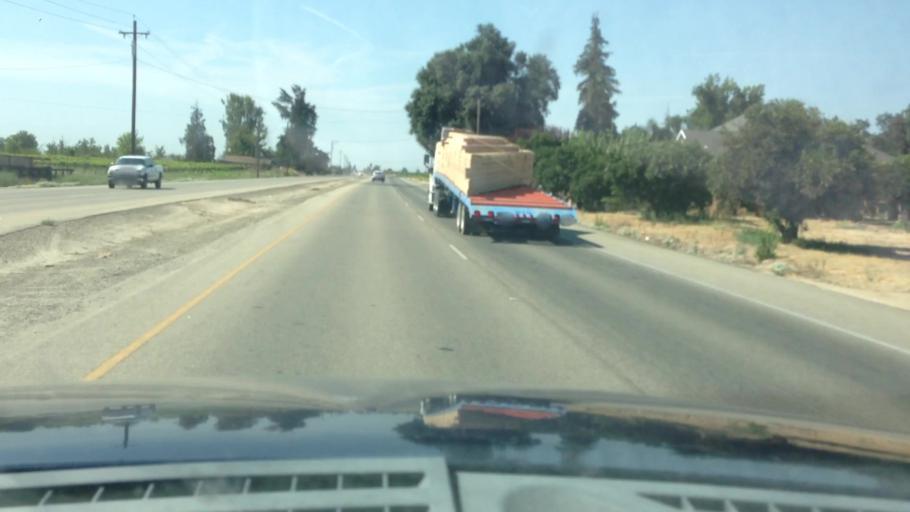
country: US
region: California
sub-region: Fresno County
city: Del Rey
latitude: 36.6412
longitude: -119.5566
